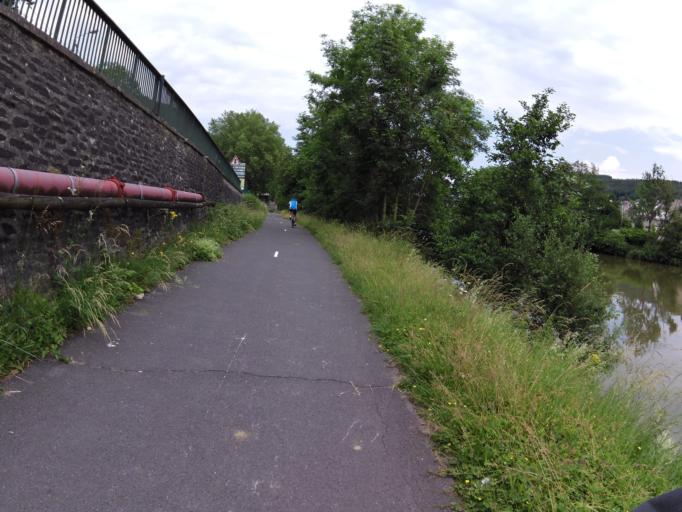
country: FR
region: Champagne-Ardenne
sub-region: Departement des Ardennes
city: Nouzonville
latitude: 49.8147
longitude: 4.7401
